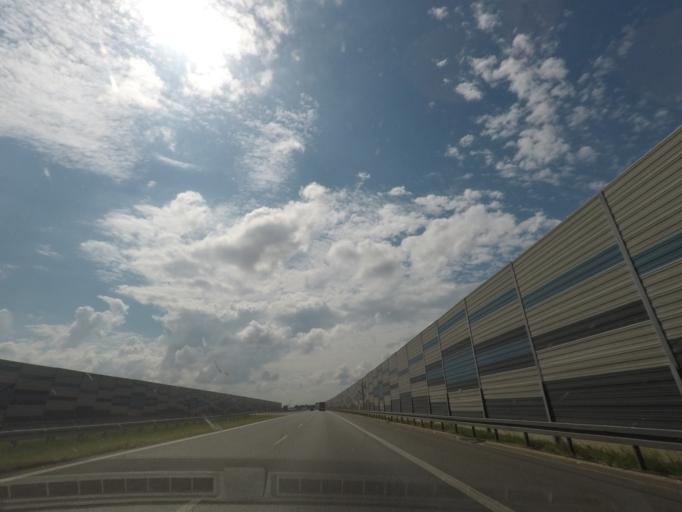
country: PL
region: Lodz Voivodeship
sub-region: Powiat leczycki
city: Piatek
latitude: 52.0169
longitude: 19.5419
